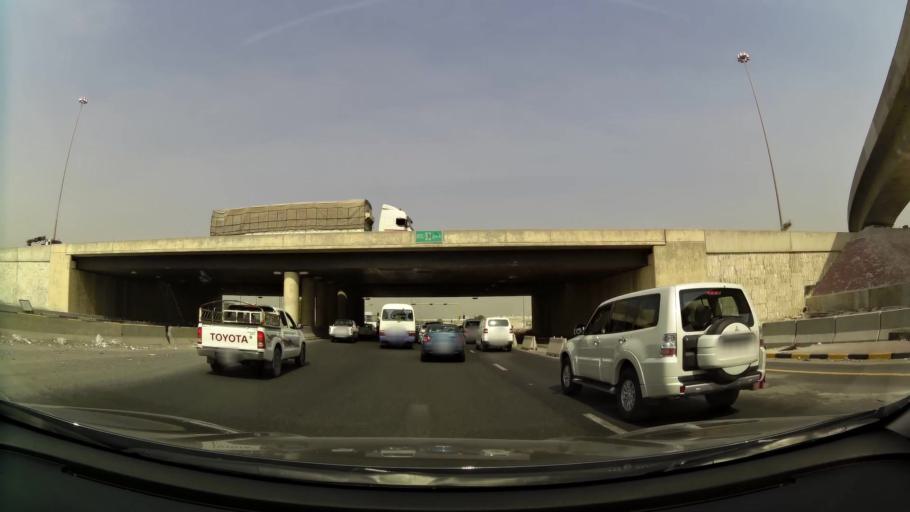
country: KW
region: Al Asimah
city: Ar Rabiyah
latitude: 29.2671
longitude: 47.9080
